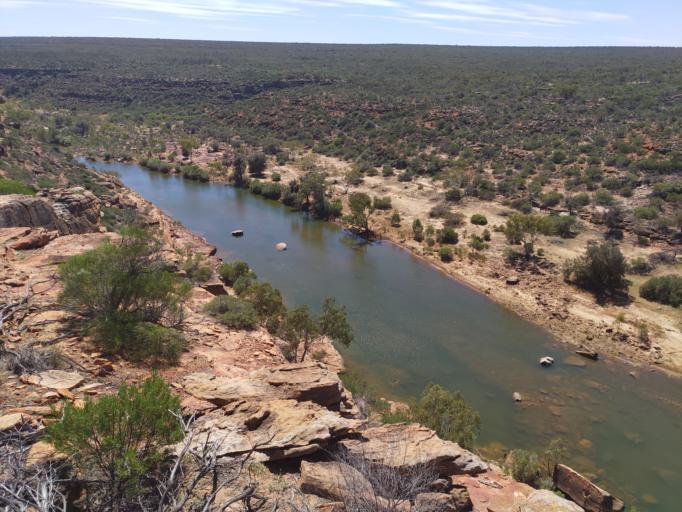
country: AU
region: Western Australia
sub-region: Northampton Shire
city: Kalbarri
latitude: -27.7889
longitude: 114.4691
